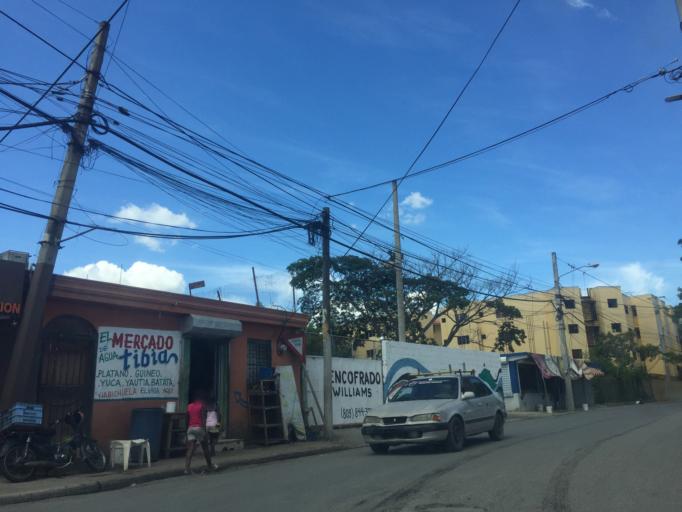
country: DO
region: Santiago
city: Santiago de los Caballeros
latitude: 19.4364
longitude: -70.6792
